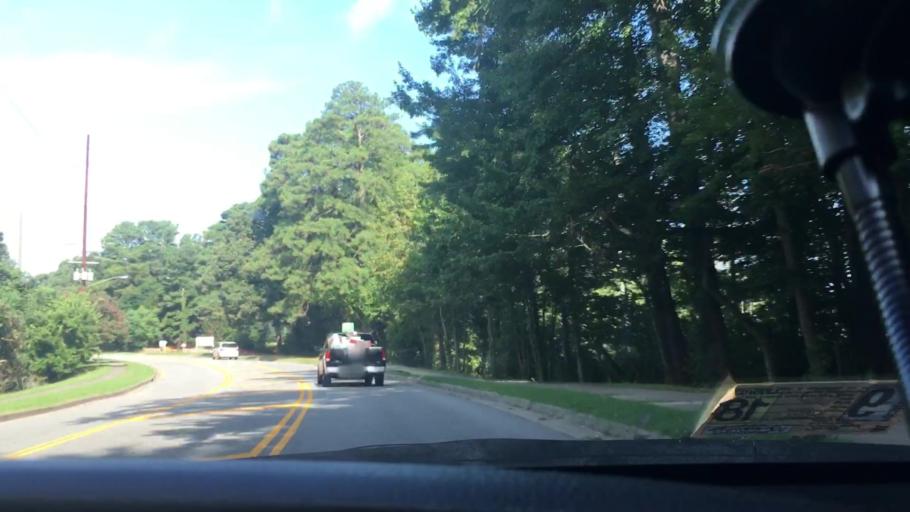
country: US
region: Virginia
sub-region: City of Virginia Beach
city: Virginia Beach
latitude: 36.8795
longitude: -76.0343
